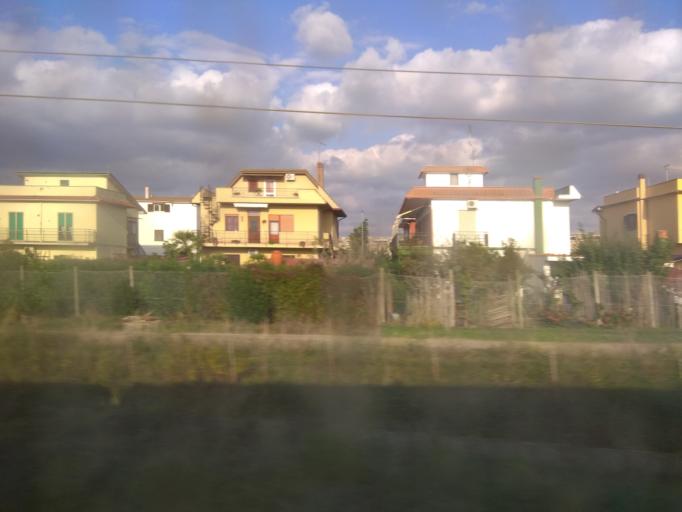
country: IT
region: Latium
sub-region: Citta metropolitana di Roma Capitale
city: Maccarese
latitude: 41.8735
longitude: 12.2429
